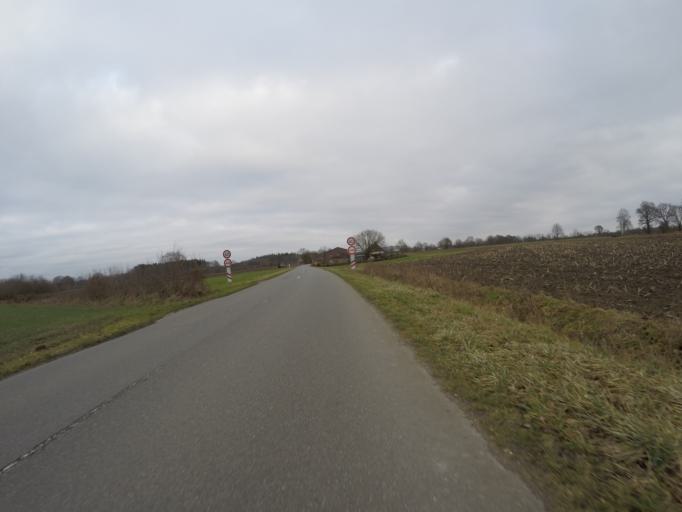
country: DE
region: Schleswig-Holstein
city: Langeln
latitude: 53.7907
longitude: 9.8413
